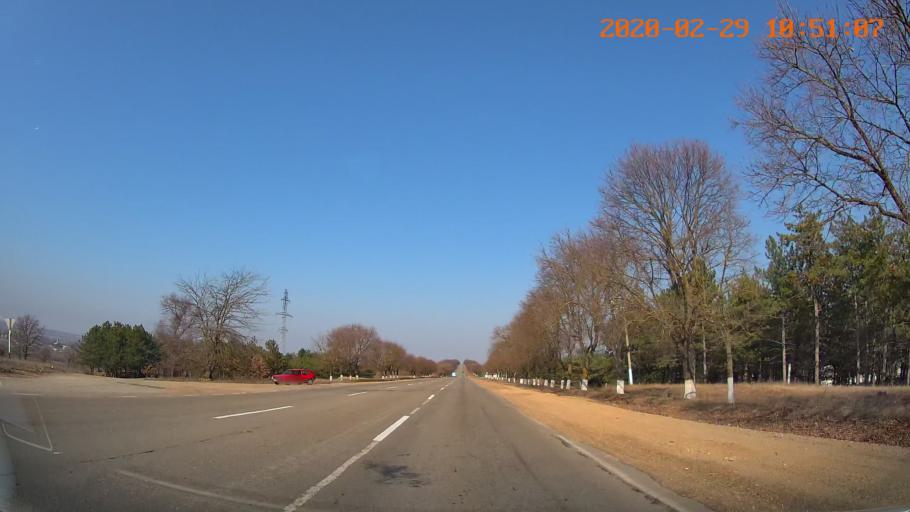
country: MD
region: Telenesti
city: Grigoriopol
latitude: 47.0899
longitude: 29.3684
